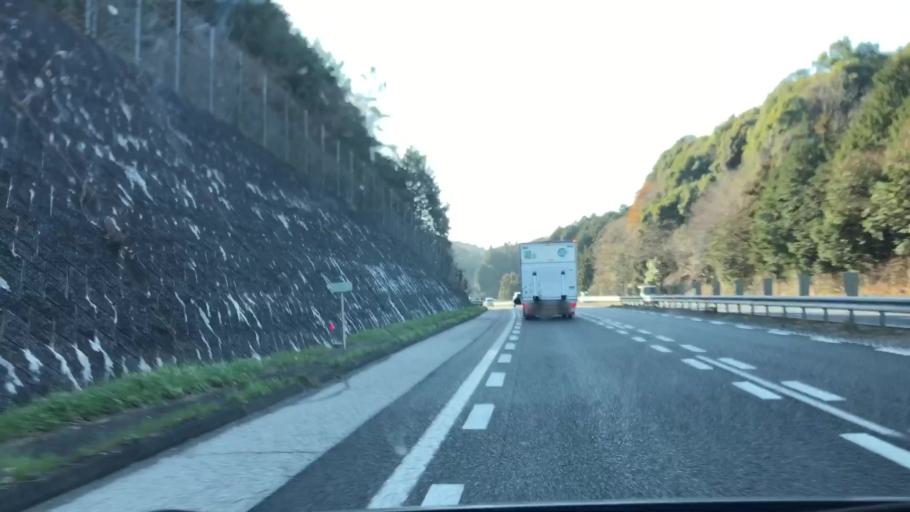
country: JP
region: Yamaguchi
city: Onoda
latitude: 34.1154
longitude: 131.1725
